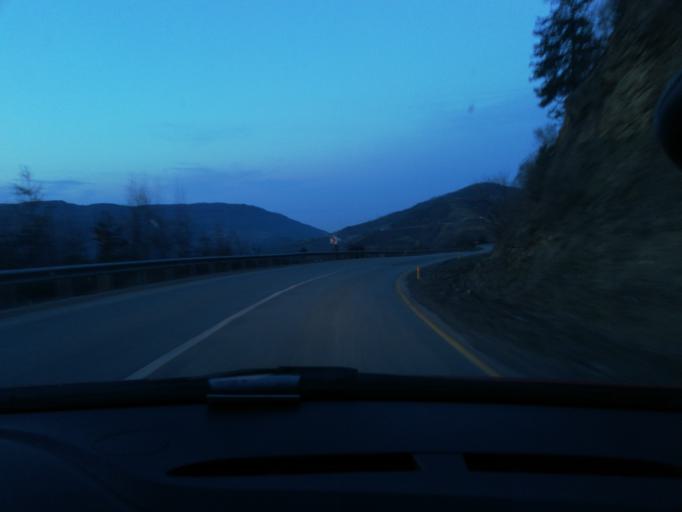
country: TR
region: Kastamonu
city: Inebolu
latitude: 41.9225
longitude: 33.7365
